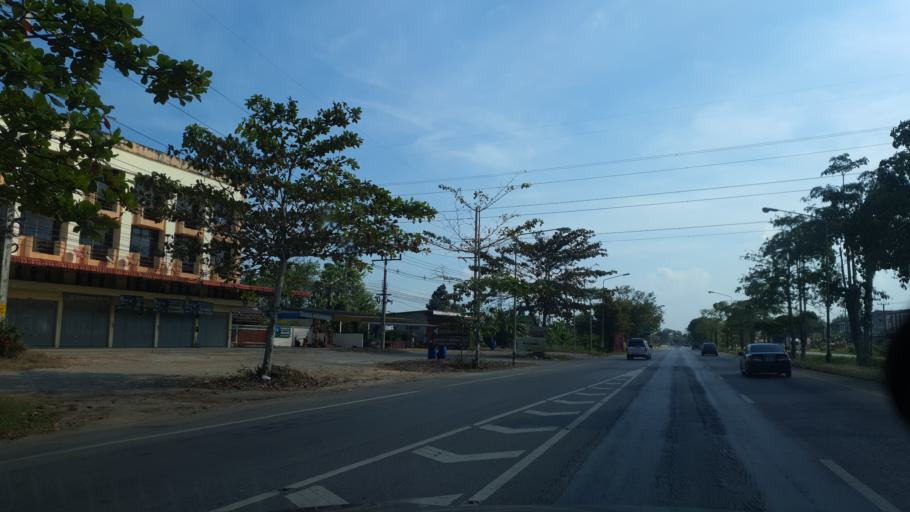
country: TH
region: Surat Thani
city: Phunphin
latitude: 9.1076
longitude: 99.1616
